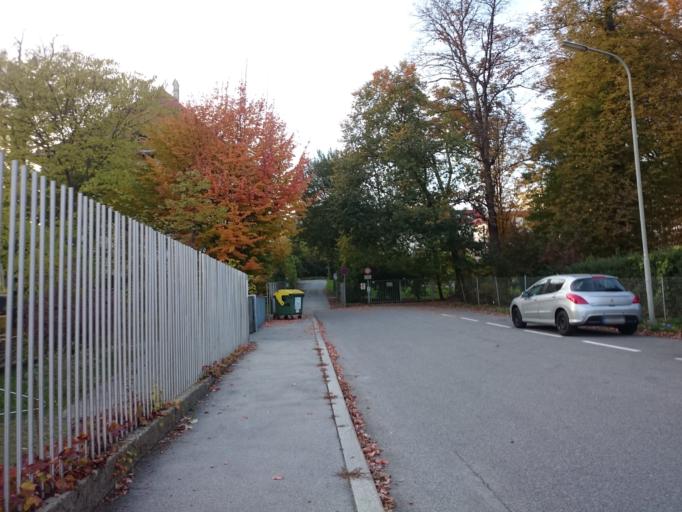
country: AT
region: Styria
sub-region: Graz Stadt
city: Graz
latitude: 47.0822
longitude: 15.4574
